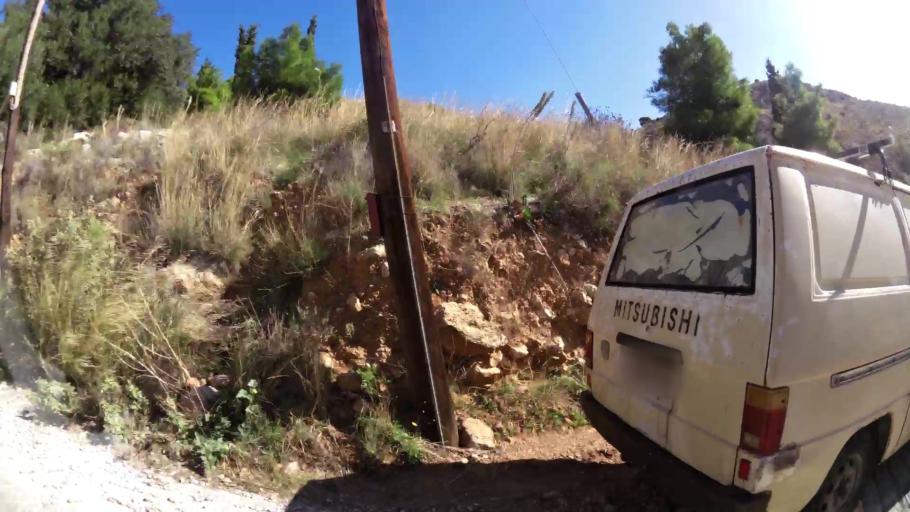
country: GR
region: Attica
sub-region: Nomos Piraios
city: Keratsini
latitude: 37.9656
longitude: 23.5966
